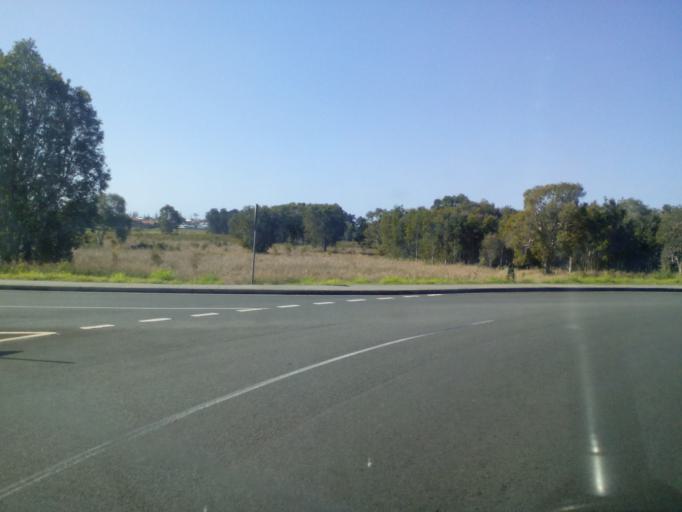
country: AU
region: New South Wales
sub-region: Tweed
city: Kingscliff
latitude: -28.2583
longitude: 153.5700
